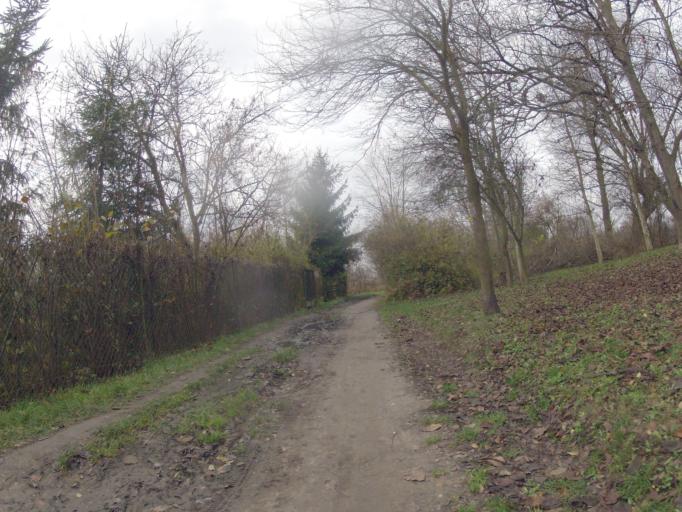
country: PL
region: Lesser Poland Voivodeship
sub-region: Powiat krakowski
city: Rzaska
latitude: 50.0766
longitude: 19.8685
